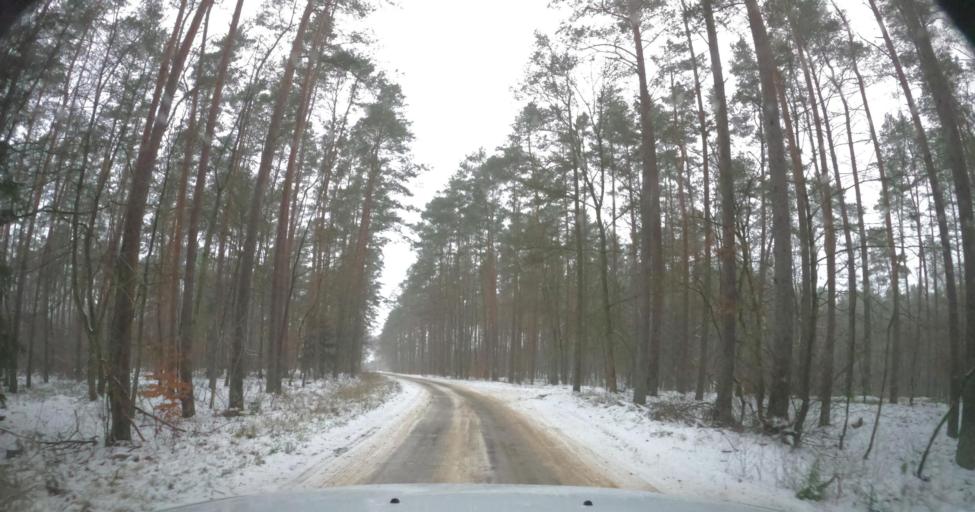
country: PL
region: West Pomeranian Voivodeship
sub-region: Powiat kamienski
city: Golczewo
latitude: 53.8405
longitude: 14.9976
